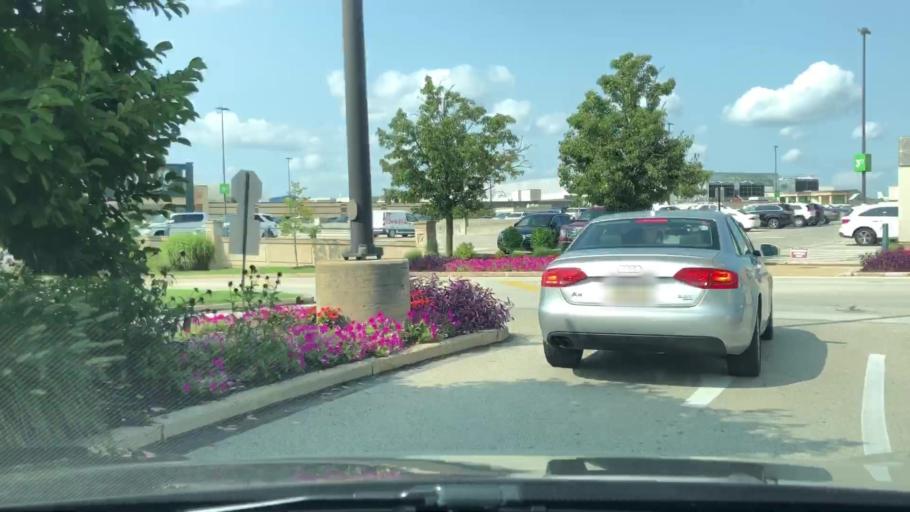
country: US
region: Pennsylvania
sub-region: Montgomery County
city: King of Prussia
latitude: 40.0860
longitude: -75.3935
